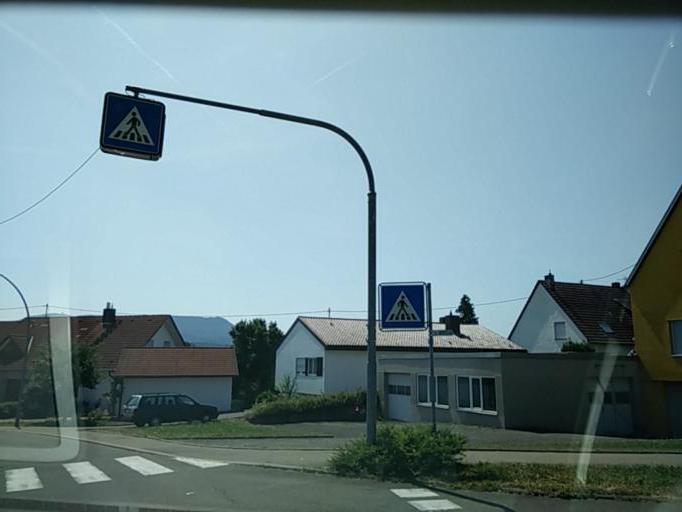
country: DE
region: Baden-Wuerttemberg
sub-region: Tuebingen Region
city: Gomaringen
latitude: 48.4571
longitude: 9.1021
